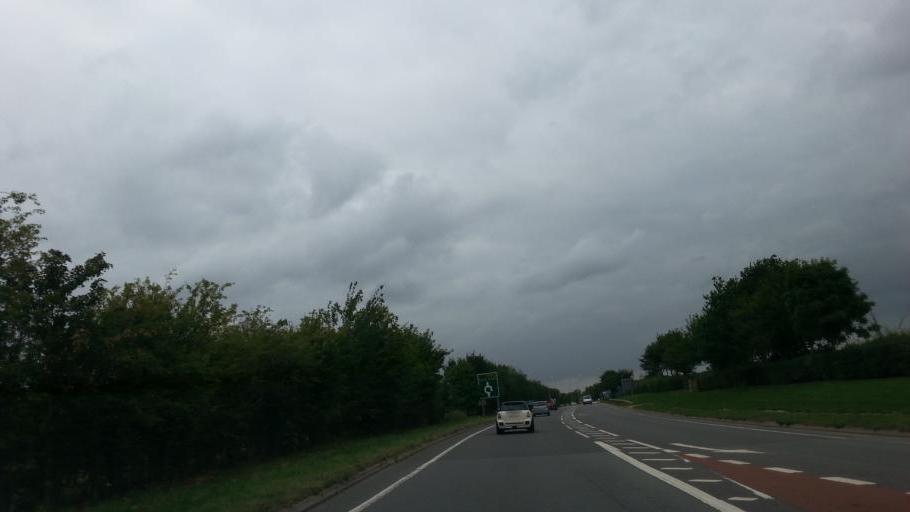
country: GB
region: England
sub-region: Essex
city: Chelmsford
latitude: 51.7619
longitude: 0.4889
